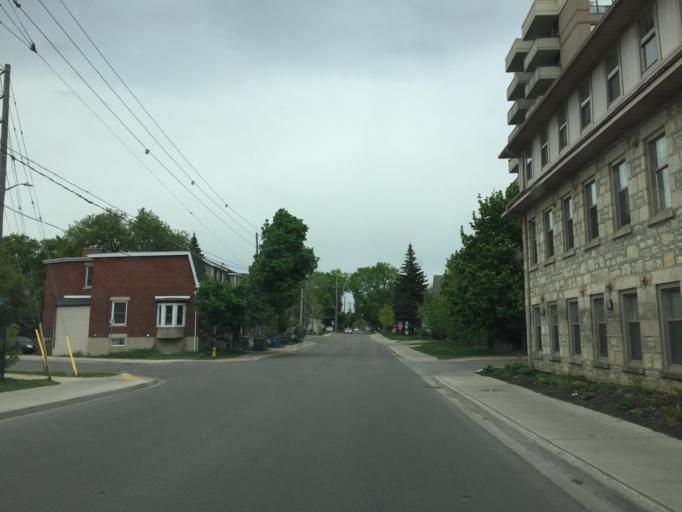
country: CA
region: Ontario
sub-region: Wellington County
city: Guelph
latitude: 43.5444
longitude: -80.2417
